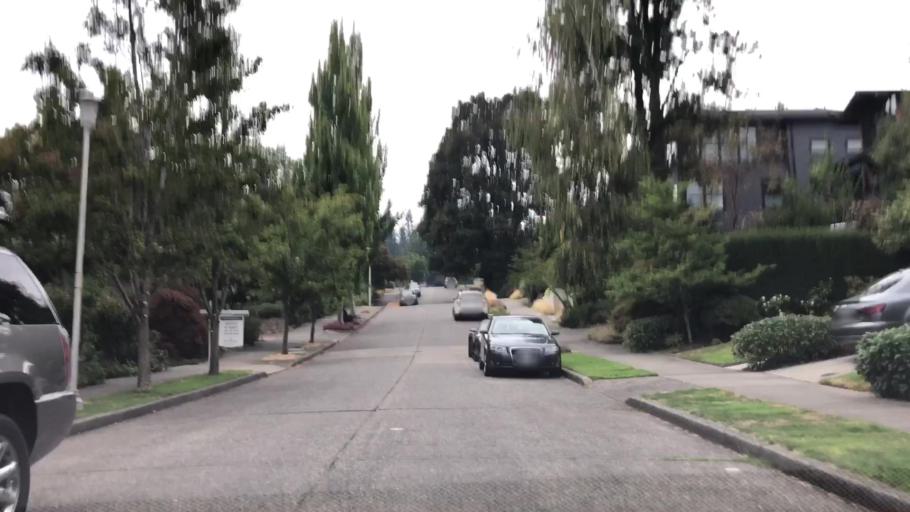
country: US
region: Washington
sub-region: King County
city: Yarrow Point
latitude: 47.6594
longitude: -122.2730
